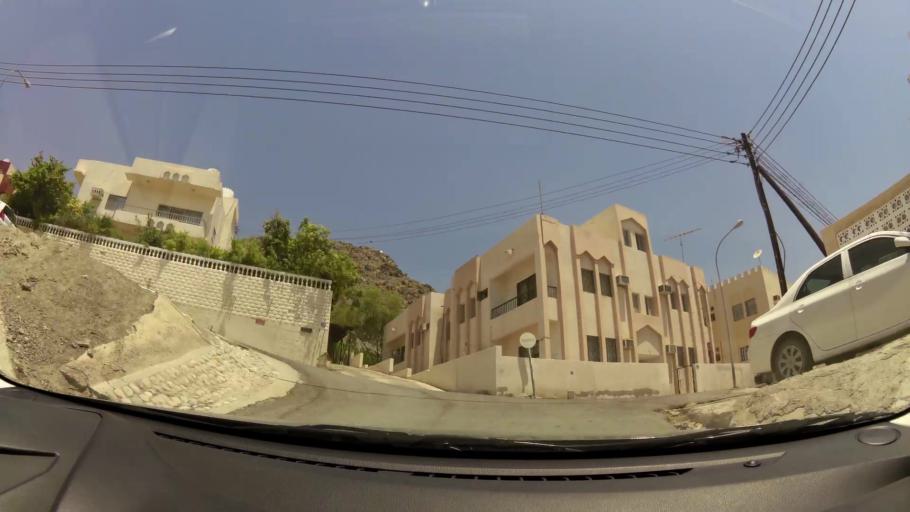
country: OM
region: Muhafazat Masqat
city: Muscat
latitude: 23.6094
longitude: 58.5361
